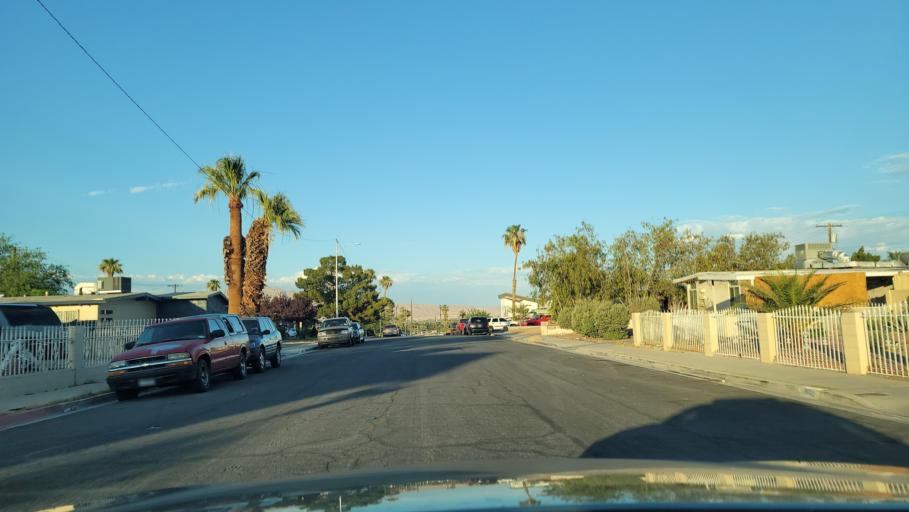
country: US
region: Nevada
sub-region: Clark County
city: Winchester
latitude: 36.1473
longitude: -115.1311
